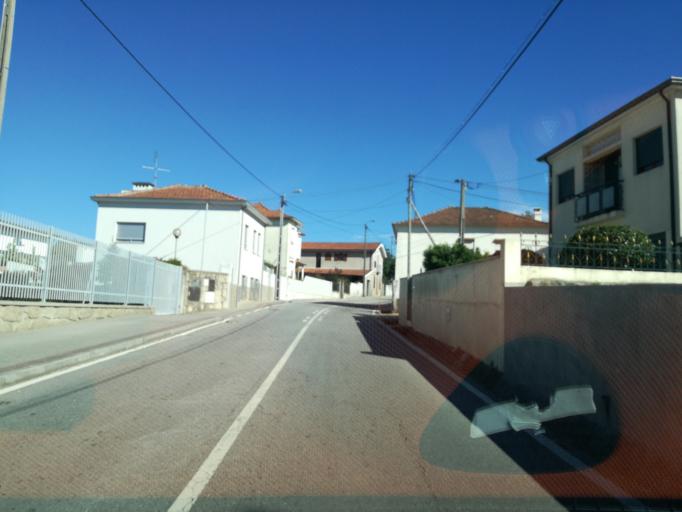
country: PT
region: Porto
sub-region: Trofa
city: Sao Romao do Coronado
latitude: 41.2778
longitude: -8.5495
